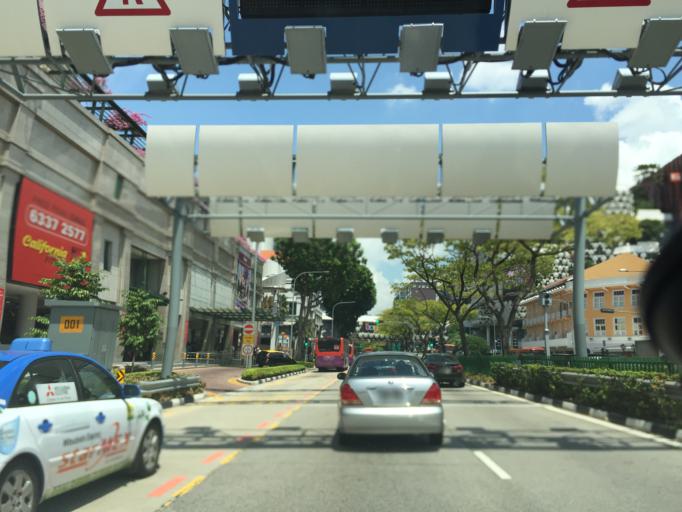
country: SG
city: Singapore
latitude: 1.3004
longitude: 103.8558
